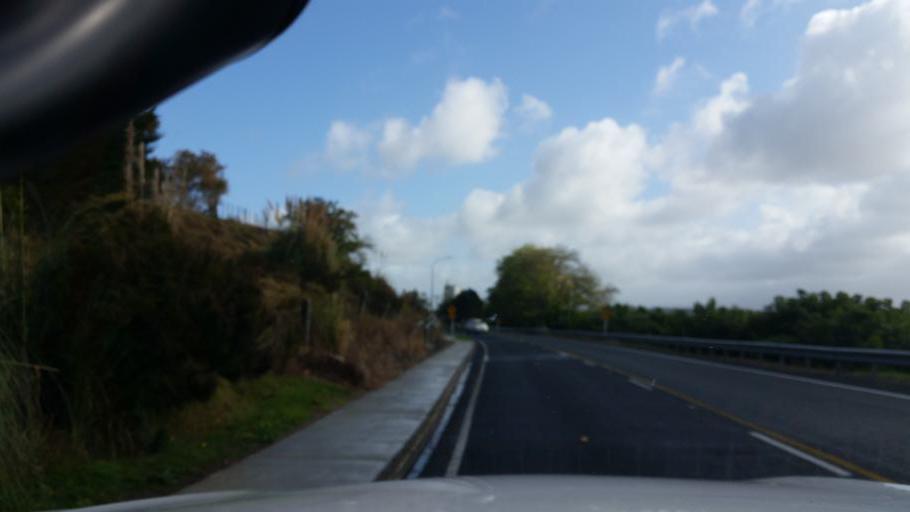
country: NZ
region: Northland
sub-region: Kaipara District
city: Dargaville
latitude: -35.9586
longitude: 173.8687
